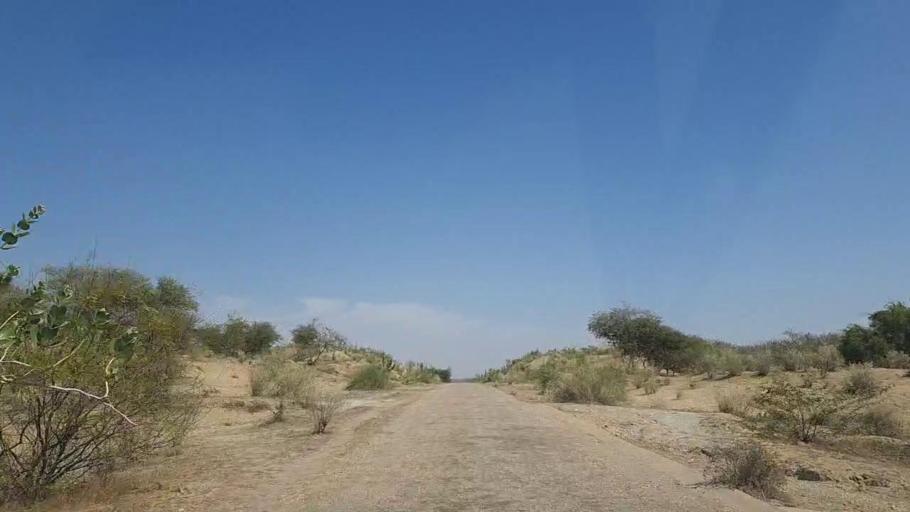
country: PK
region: Sindh
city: Mithi
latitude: 24.8318
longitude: 69.7119
